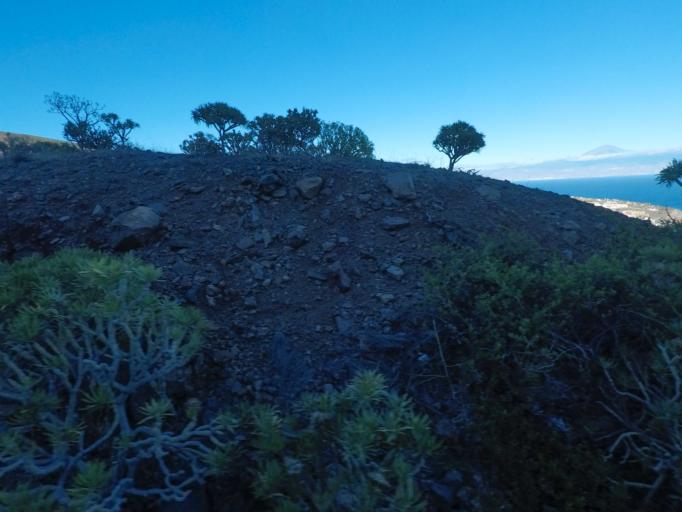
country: ES
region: Canary Islands
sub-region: Provincia de Santa Cruz de Tenerife
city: San Sebastian de la Gomera
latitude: 28.0839
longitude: -17.1324
